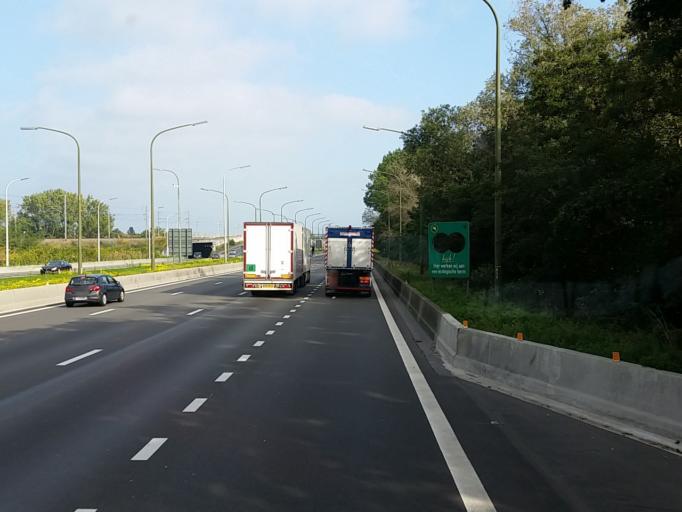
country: BE
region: Flanders
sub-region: Provincie Antwerpen
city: Brasschaat
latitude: 51.2675
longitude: 4.4524
